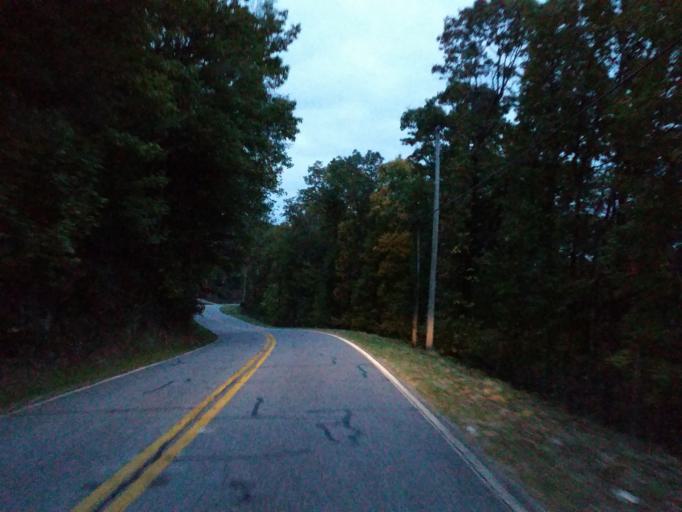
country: US
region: Georgia
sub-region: Lumpkin County
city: Dahlonega
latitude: 34.6355
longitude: -83.9568
